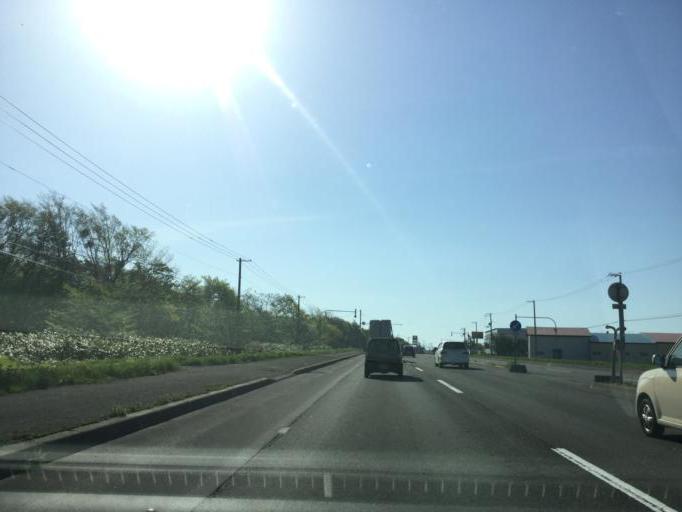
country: JP
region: Hokkaido
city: Kitahiroshima
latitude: 43.0093
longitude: 141.5176
